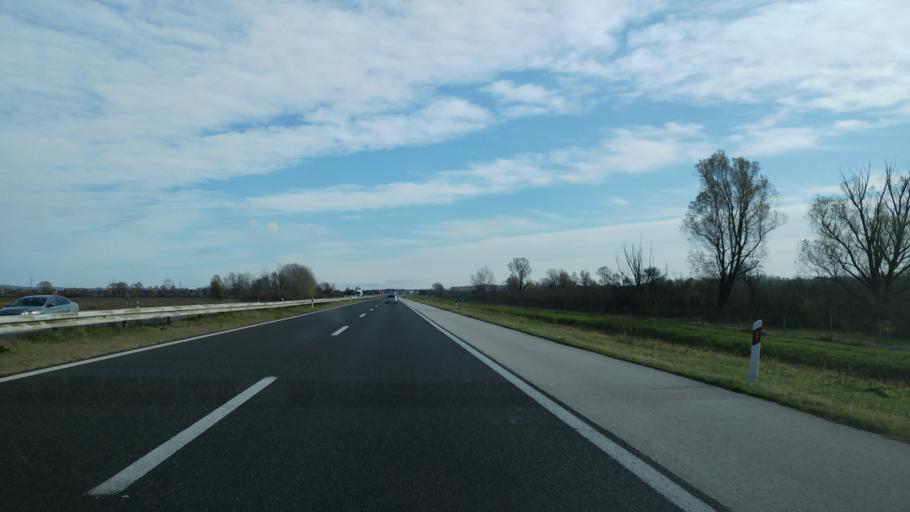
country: HR
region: Sisacko-Moslavacka
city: Repusnica
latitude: 45.4842
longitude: 16.7091
